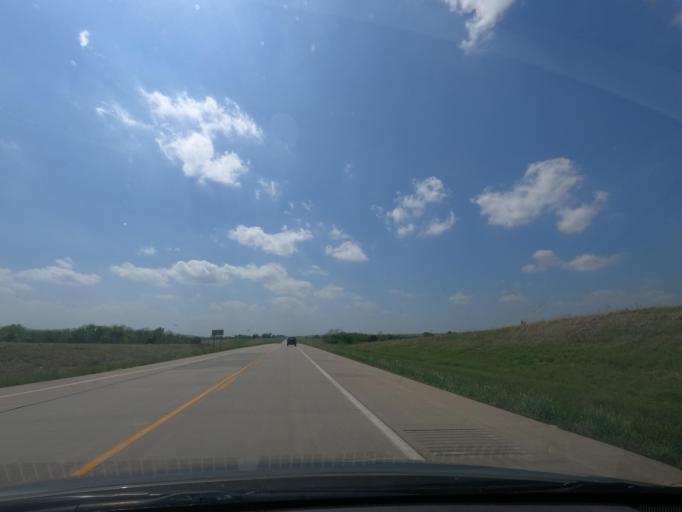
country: US
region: Kansas
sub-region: Elk County
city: Howard
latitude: 37.6278
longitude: -96.0985
